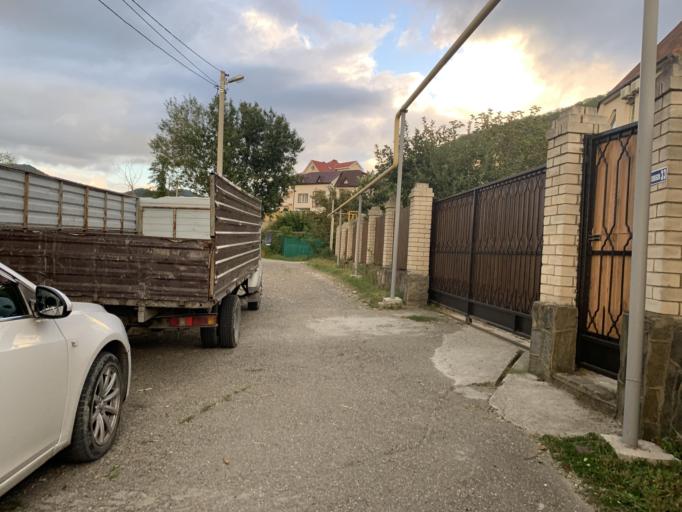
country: RU
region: Krasnodarskiy
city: Nebug
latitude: 44.1663
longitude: 39.0032
